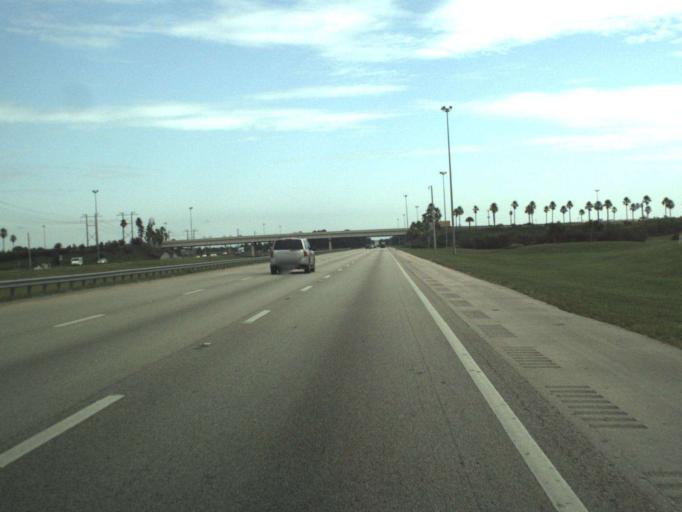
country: US
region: Florida
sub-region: Saint Lucie County
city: Port Saint Lucie
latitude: 27.3074
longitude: -80.4139
